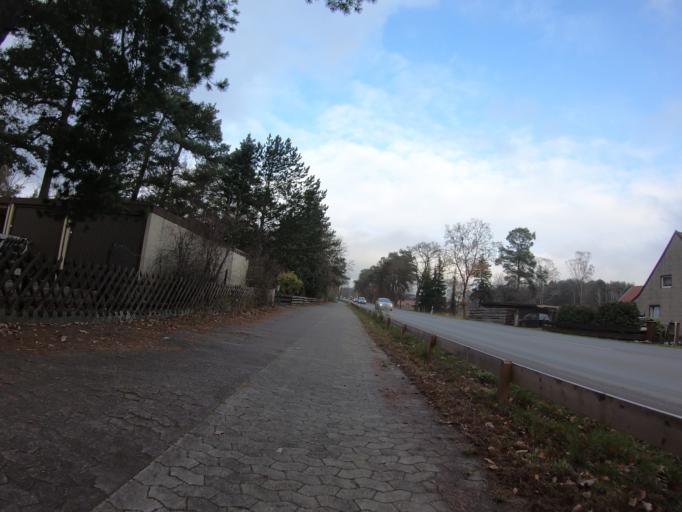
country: DE
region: Lower Saxony
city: Wagenhoff
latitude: 52.5583
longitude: 10.5141
